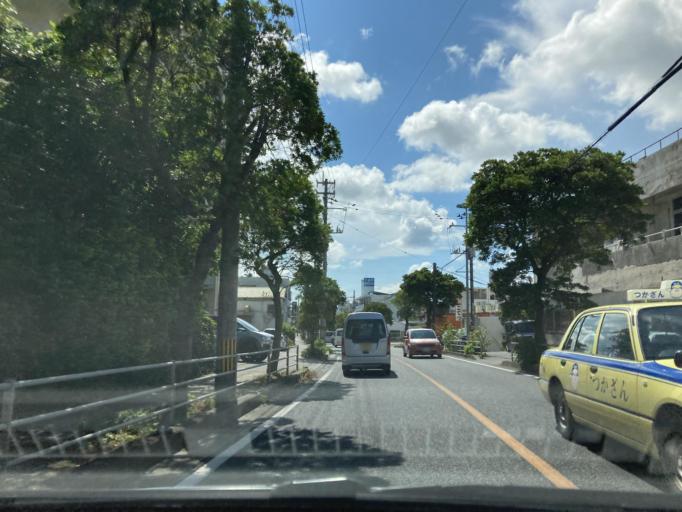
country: JP
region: Okinawa
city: Tomigusuku
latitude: 26.1851
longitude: 127.7118
